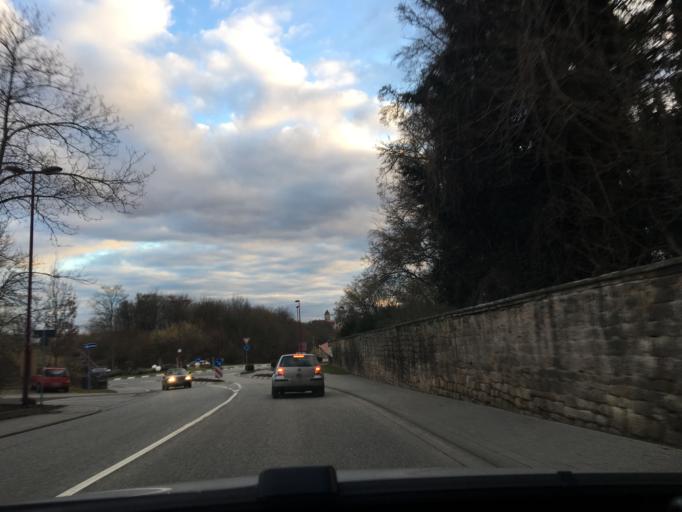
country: DE
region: Rheinland-Pfalz
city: Kirchheimbolanden
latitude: 49.6683
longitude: 8.0162
